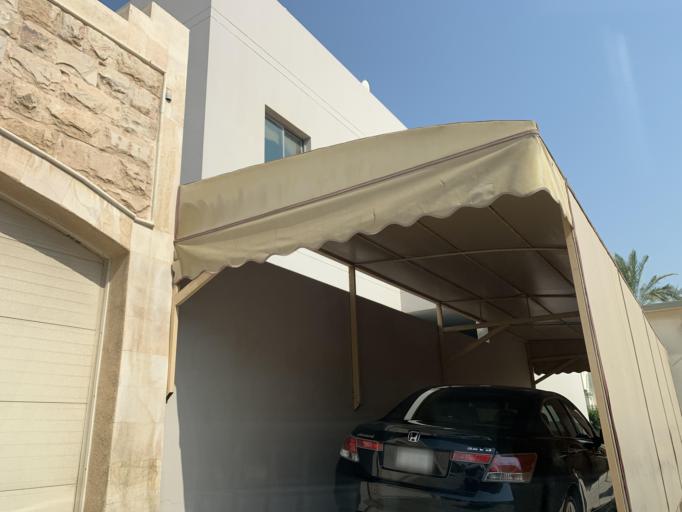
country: BH
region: Northern
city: Madinat `Isa
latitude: 26.1909
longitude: 50.5114
